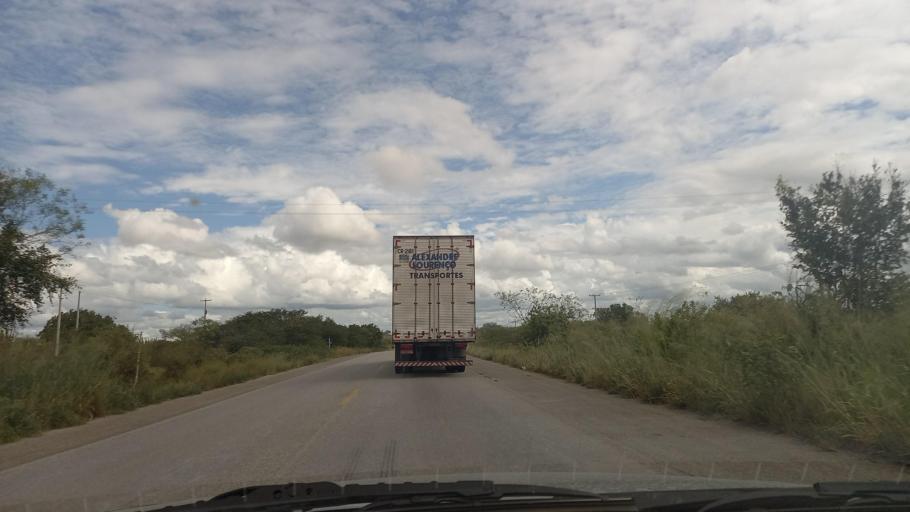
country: BR
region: Pernambuco
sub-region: Cachoeirinha
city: Cachoeirinha
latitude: -8.3935
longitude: -36.1797
